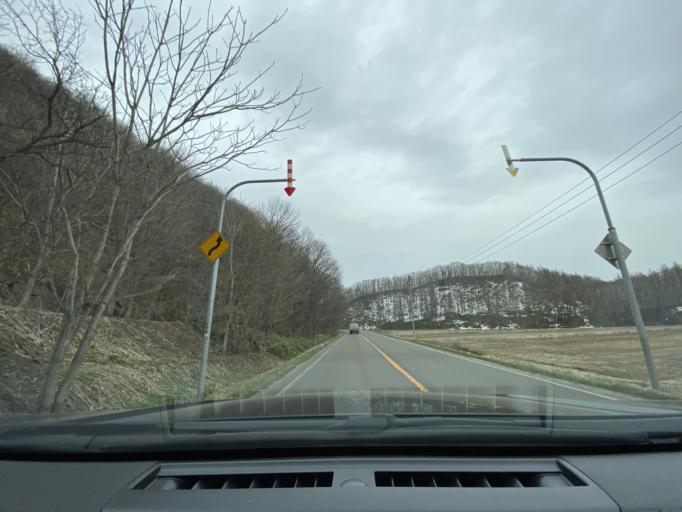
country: JP
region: Hokkaido
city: Nayoro
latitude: 44.0901
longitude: 142.4458
